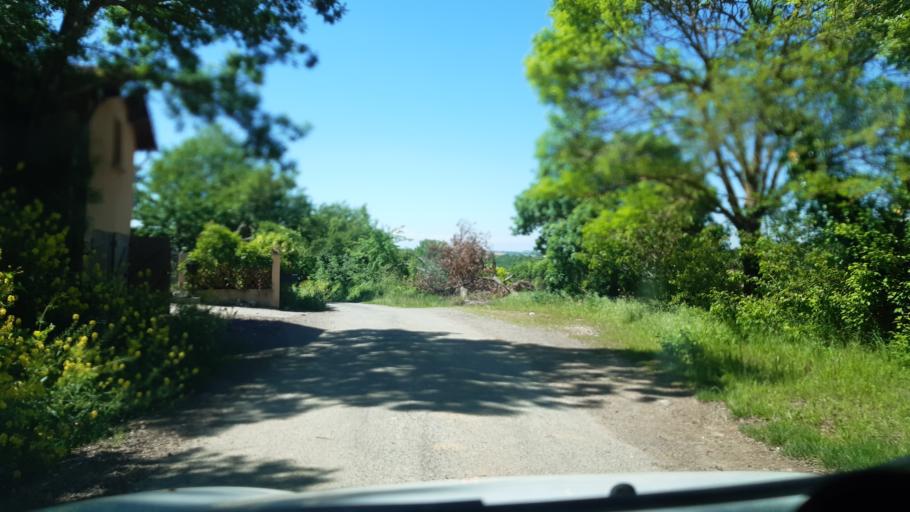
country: FR
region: Midi-Pyrenees
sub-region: Departement du Gers
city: Samatan
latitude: 43.5060
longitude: 1.0075
